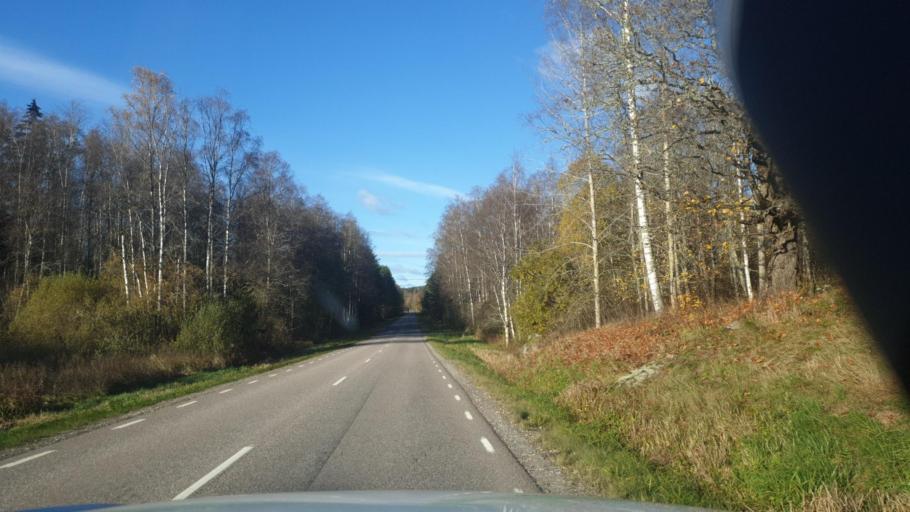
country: SE
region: Vaermland
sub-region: Arvika Kommun
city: Arvika
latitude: 59.6533
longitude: 12.8899
